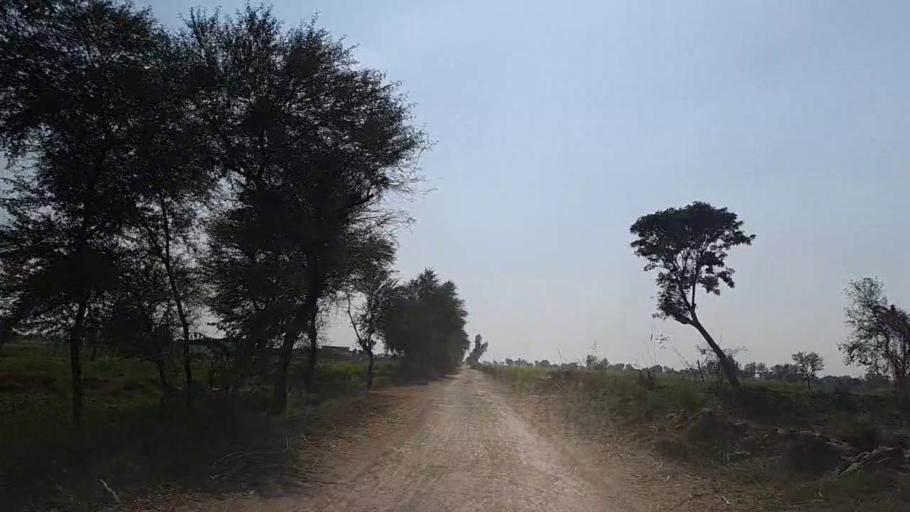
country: PK
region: Sindh
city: Daur
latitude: 26.4602
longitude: 68.2632
